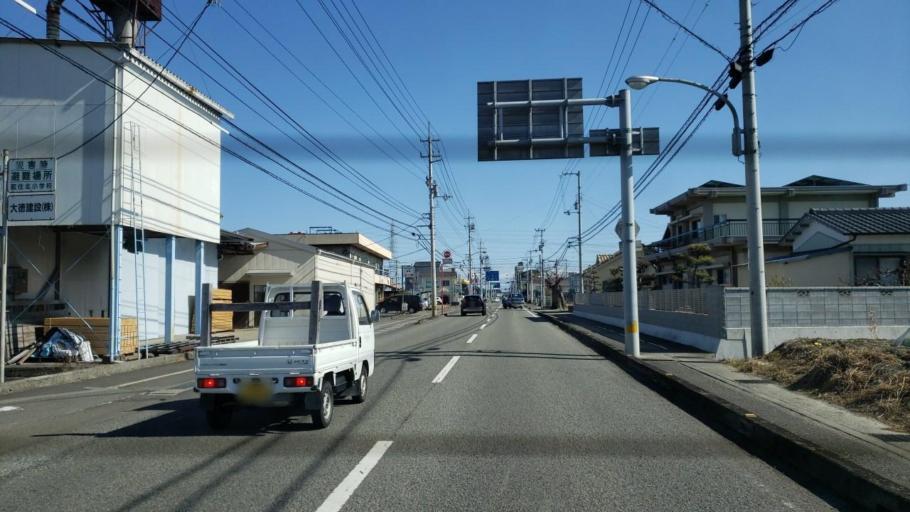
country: JP
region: Tokushima
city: Tokushima-shi
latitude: 34.1329
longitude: 134.5157
